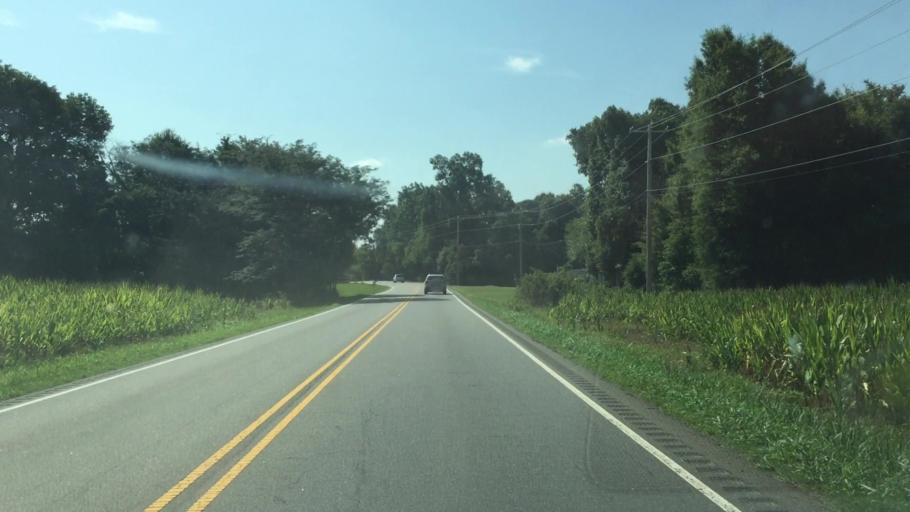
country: US
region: North Carolina
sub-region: Union County
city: Fairview
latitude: 35.1547
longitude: -80.5610
